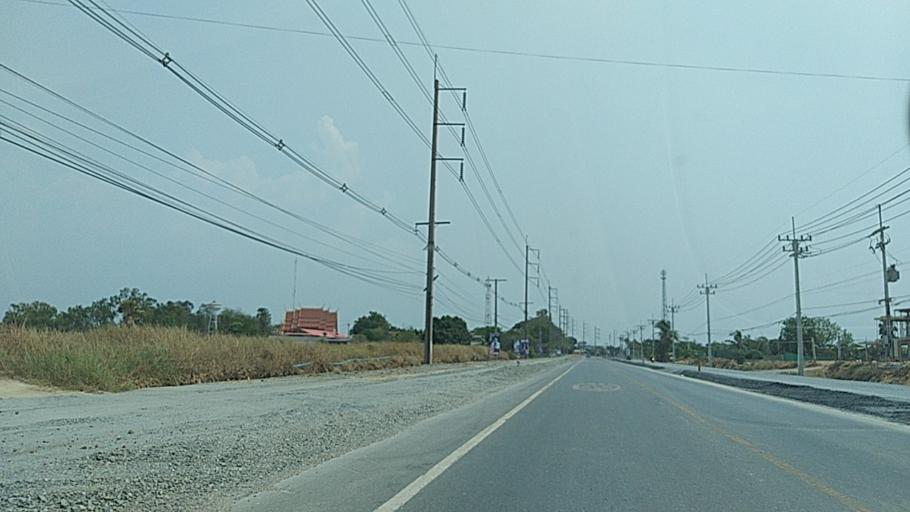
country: TH
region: Chachoengsao
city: Ban Pho
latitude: 13.5442
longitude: 101.1449
